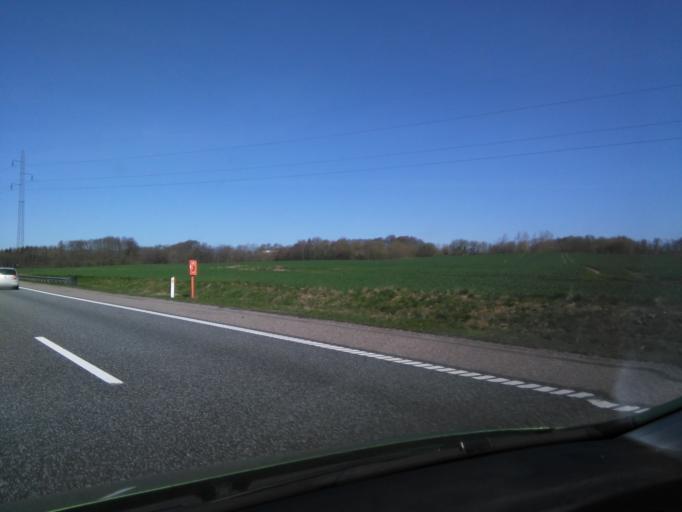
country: DK
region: Central Jutland
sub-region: Hedensted Kommune
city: Torring
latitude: 55.8354
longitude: 9.4533
